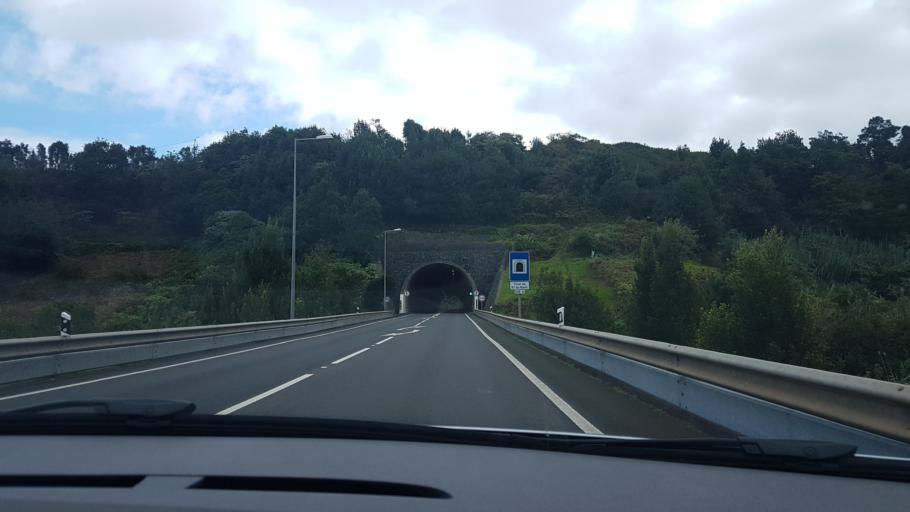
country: PT
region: Madeira
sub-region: Santana
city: Santana
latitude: 32.8096
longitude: -16.8791
